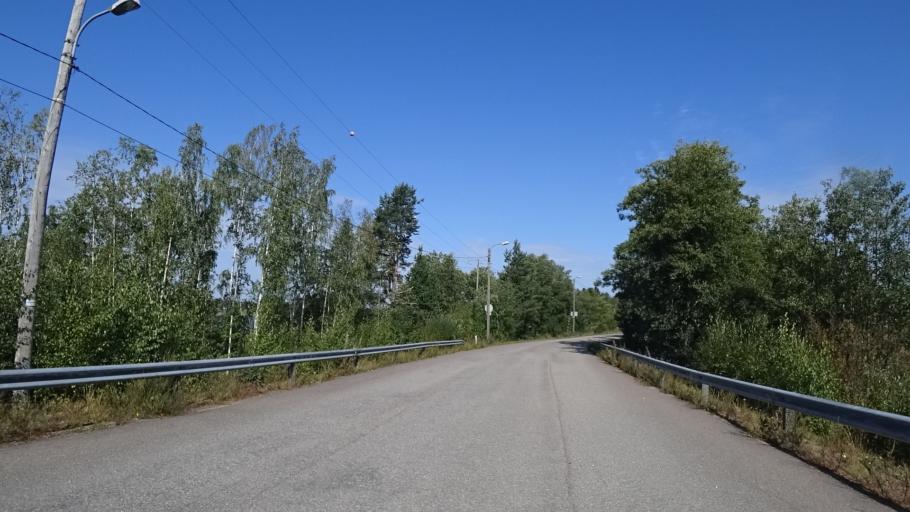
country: FI
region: Kymenlaakso
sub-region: Kotka-Hamina
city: Hamina
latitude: 60.5538
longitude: 27.1997
